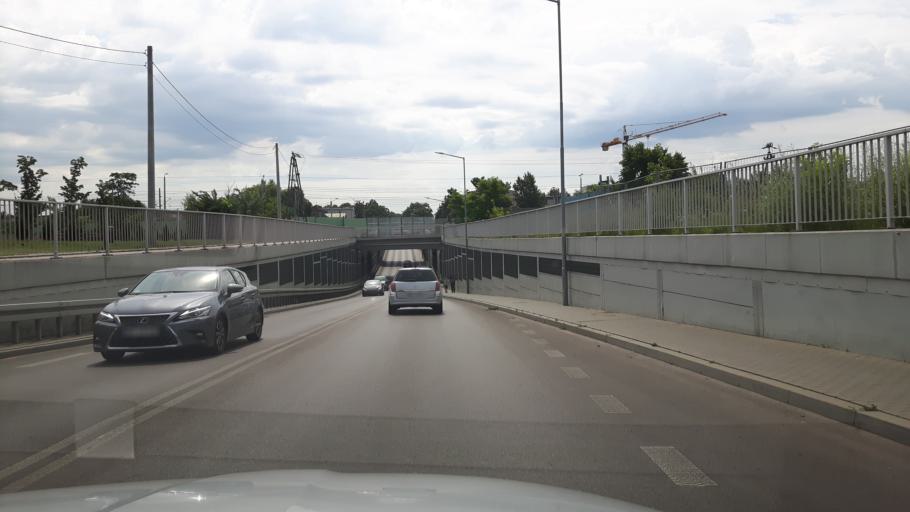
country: PL
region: Masovian Voivodeship
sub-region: Powiat wolominski
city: Nowe Lipiny
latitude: 52.3558
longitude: 21.2562
